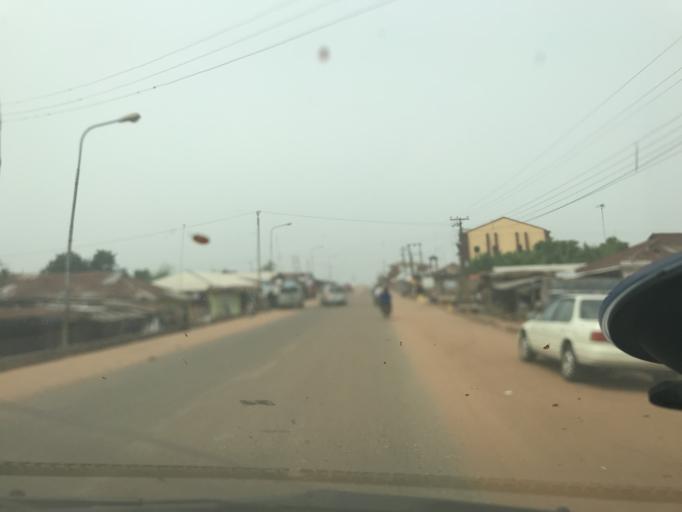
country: NG
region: Ogun
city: Ilaro
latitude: 6.8897
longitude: 3.0167
